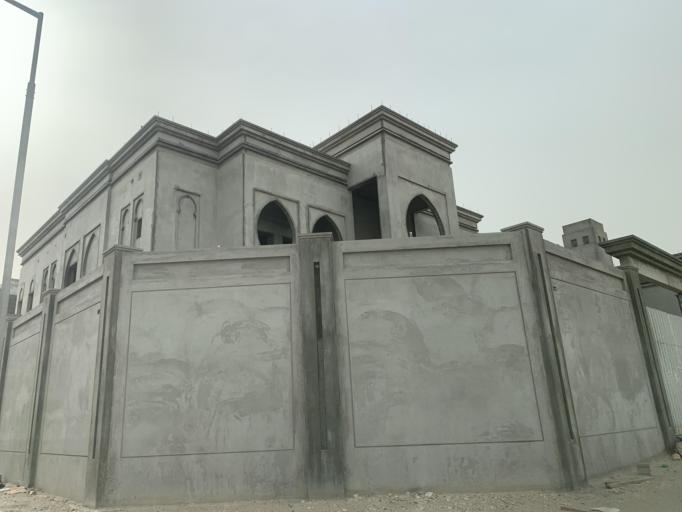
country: BH
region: Northern
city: Ar Rifa'
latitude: 26.1446
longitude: 50.5280
